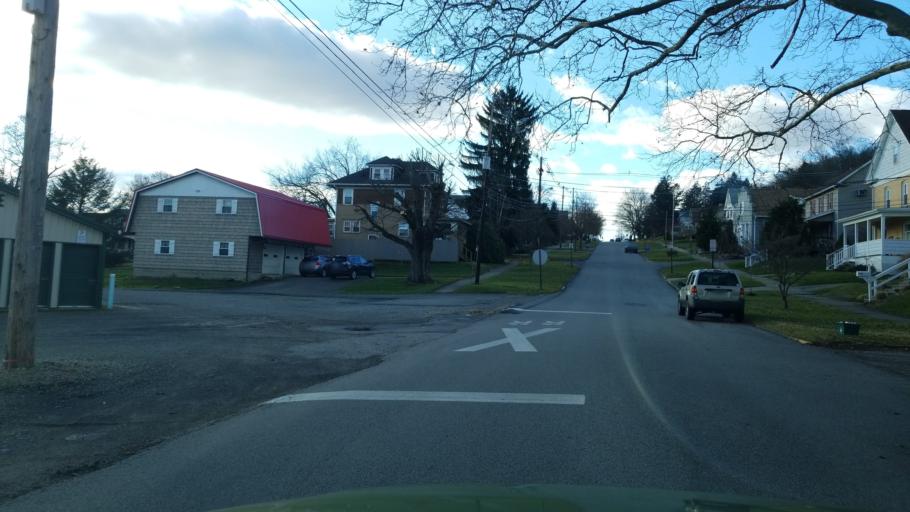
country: US
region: Pennsylvania
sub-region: Indiana County
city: Indiana
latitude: 40.6245
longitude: -79.1612
